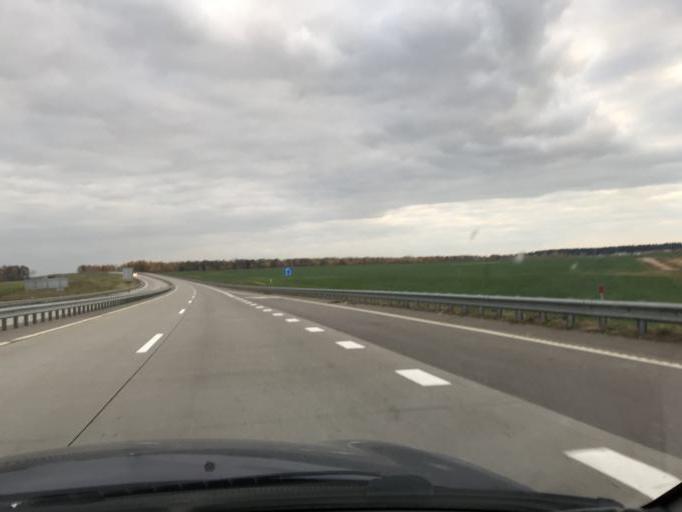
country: BY
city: Fanipol
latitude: 53.7734
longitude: 27.3599
